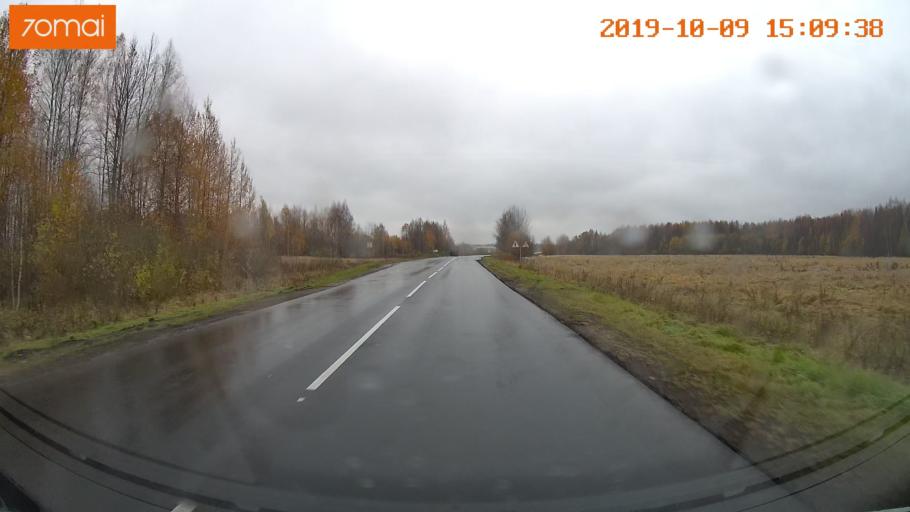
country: RU
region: Kostroma
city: Susanino
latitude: 58.1887
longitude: 41.6493
